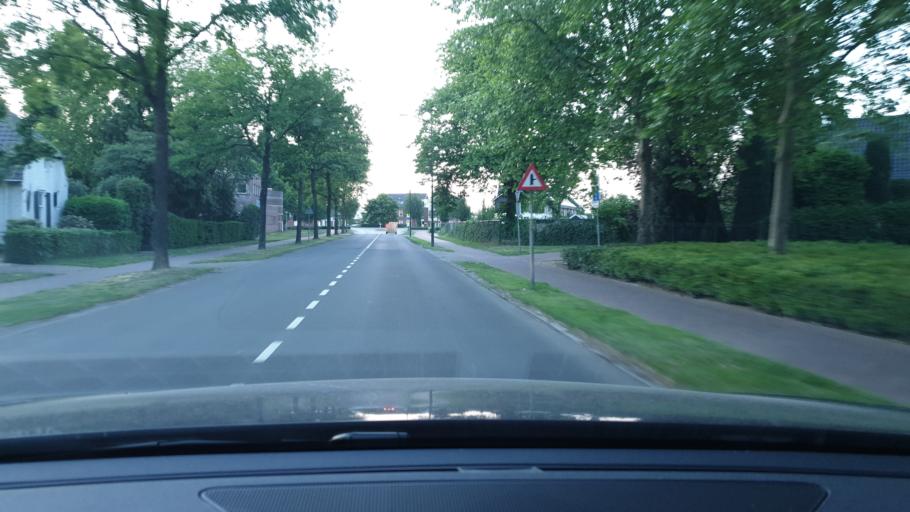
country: NL
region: North Brabant
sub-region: Gemeente Waalre
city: Waalre
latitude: 51.3913
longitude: 5.4443
